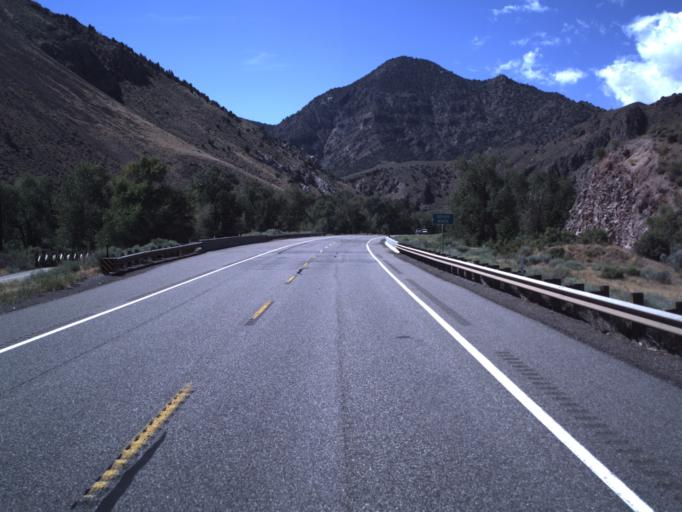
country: US
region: Utah
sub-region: Sevier County
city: Monroe
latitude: 38.5809
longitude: -112.2581
